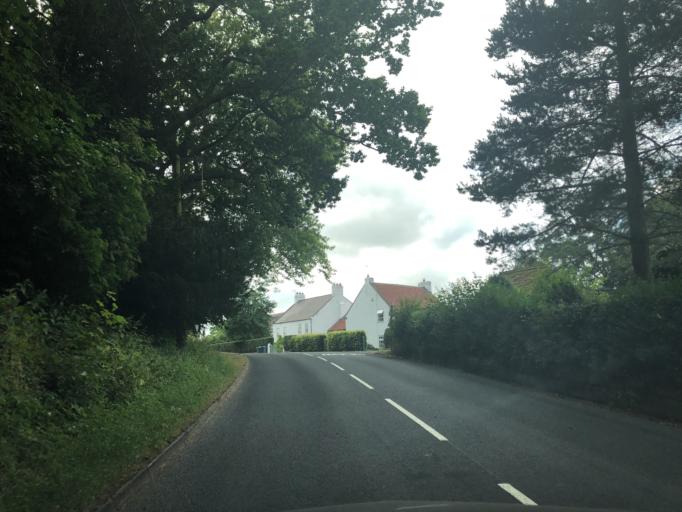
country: GB
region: England
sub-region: Stockton-on-Tees
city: Yarm
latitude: 54.4611
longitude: -1.3176
